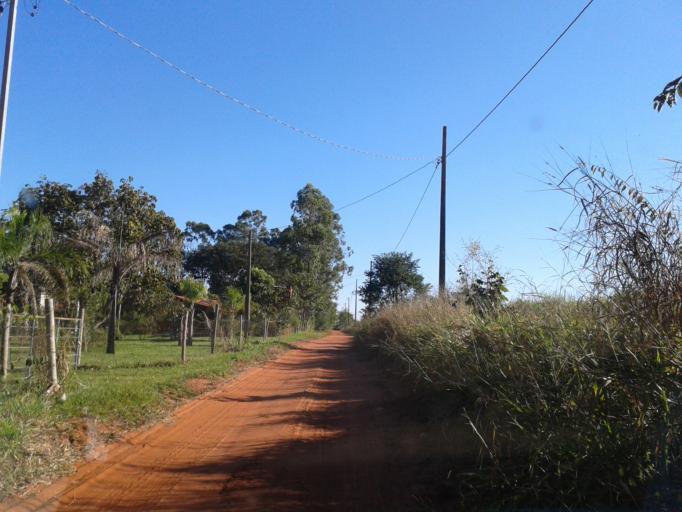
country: BR
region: Minas Gerais
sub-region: Santa Vitoria
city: Santa Vitoria
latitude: -19.0099
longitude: -50.3837
